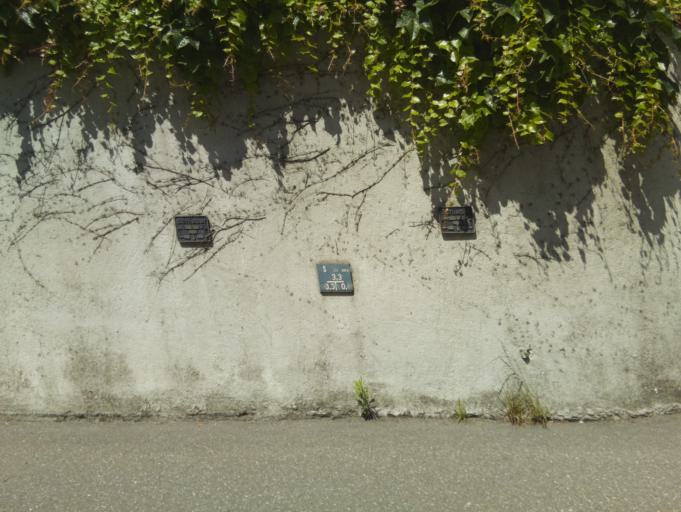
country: CH
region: Glarus
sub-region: Glarus
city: Netstal
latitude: 47.0607
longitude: 9.0530
